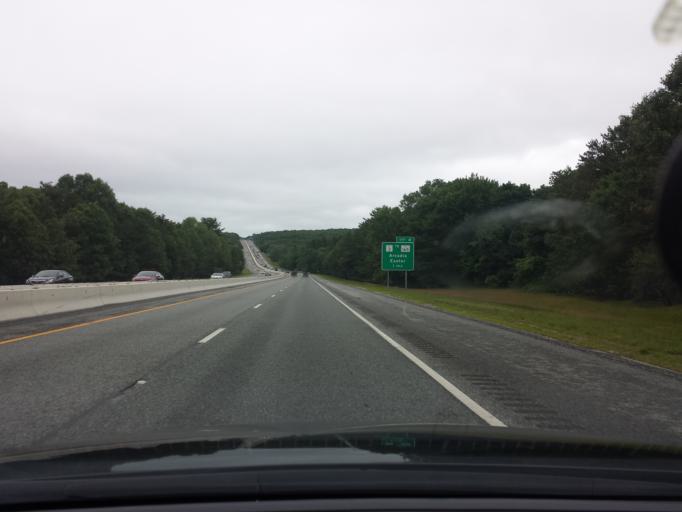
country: US
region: Rhode Island
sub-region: Washington County
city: Hope Valley
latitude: 41.5216
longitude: -71.6864
